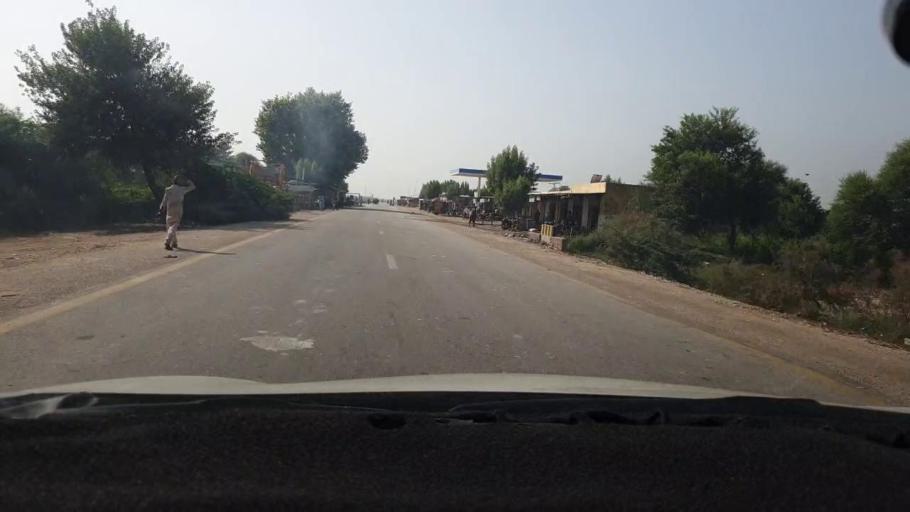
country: PK
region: Sindh
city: Sanghar
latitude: 25.9896
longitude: 68.9658
